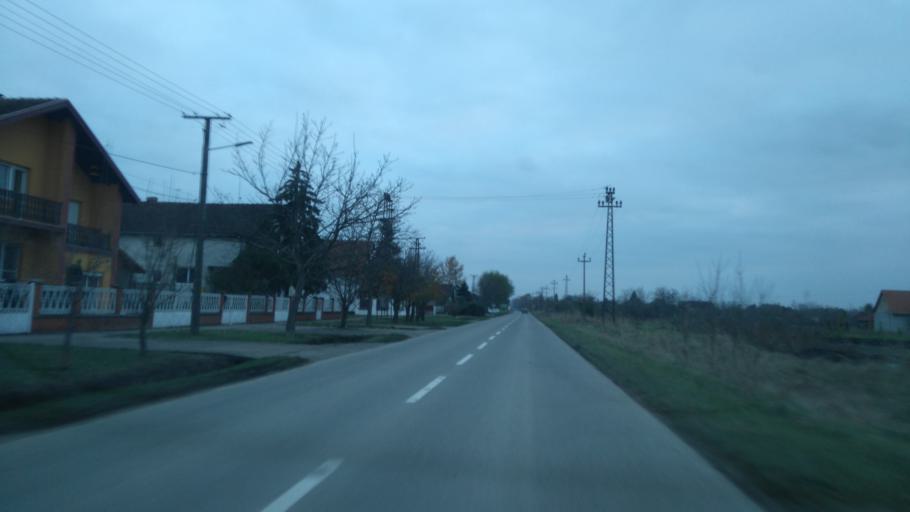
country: RS
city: Mol
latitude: 45.7743
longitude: 20.1284
